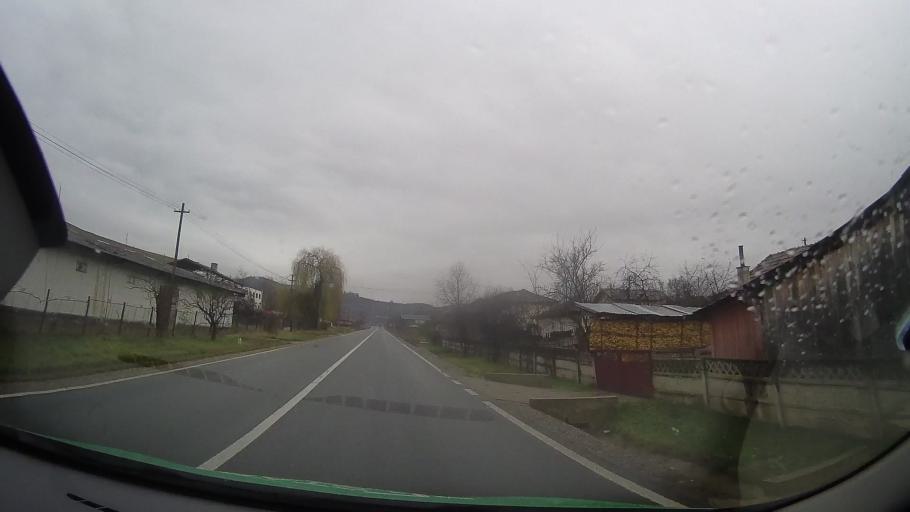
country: RO
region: Bistrita-Nasaud
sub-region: Comuna Teaca
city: Teaca
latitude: 46.9173
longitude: 24.4943
